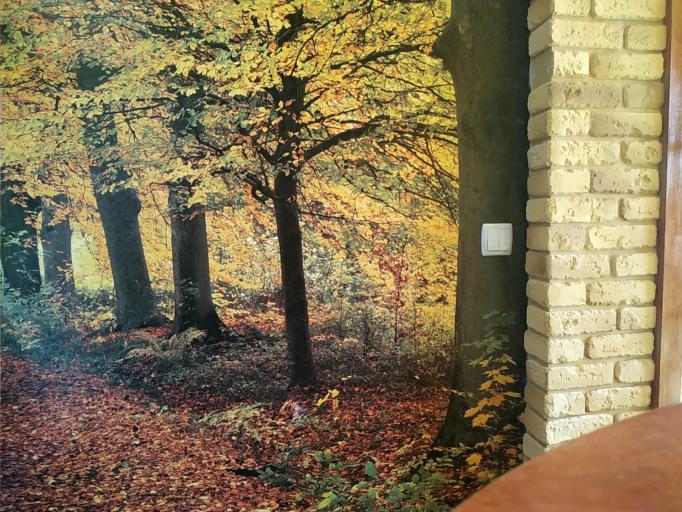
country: RU
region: Jaroslavl
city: Kukoboy
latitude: 58.9286
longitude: 39.6689
